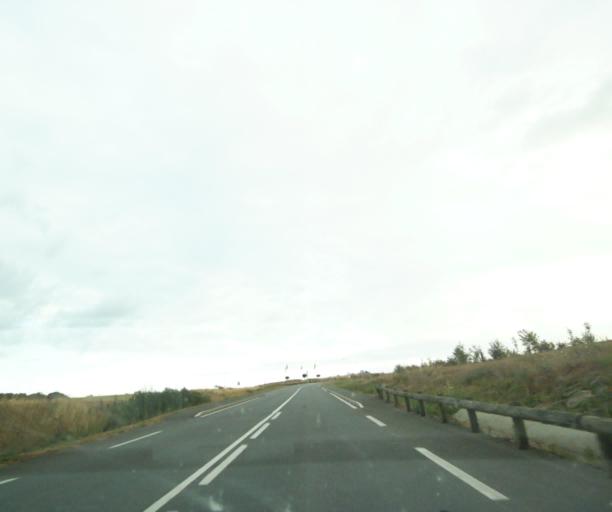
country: FR
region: Pays de la Loire
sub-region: Departement de la Vendee
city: Saint-Hilaire-de-Talmont
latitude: 46.4594
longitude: -1.6062
